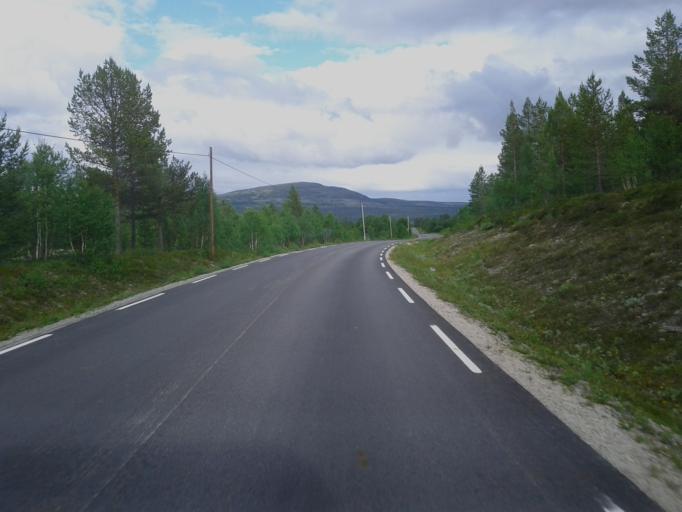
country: NO
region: Sor-Trondelag
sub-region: Roros
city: Roros
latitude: 62.3075
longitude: 11.6891
